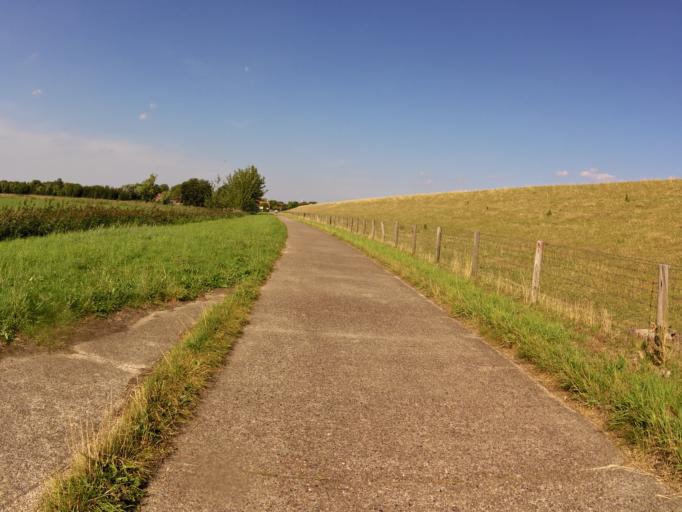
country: DE
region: Lower Saxony
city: Ovelgonne
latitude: 53.3905
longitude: 8.4593
